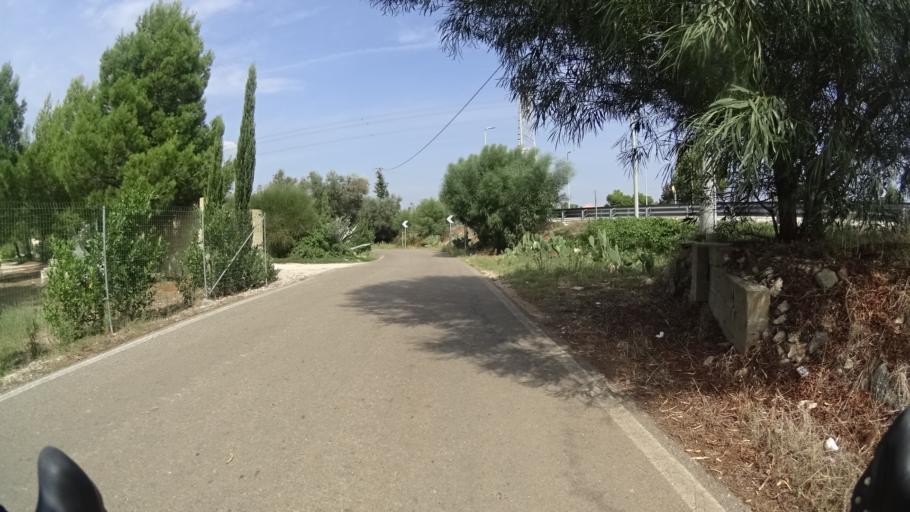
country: IT
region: Apulia
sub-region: Provincia di Lecce
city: Porto Cesareo
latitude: 40.2759
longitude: 17.9374
